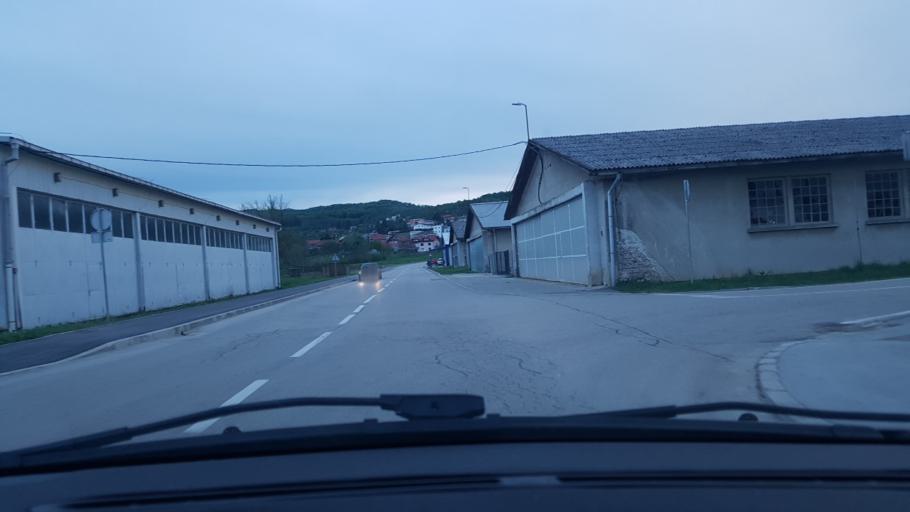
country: HR
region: Zagrebacka
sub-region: Grad Samobor
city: Samobor
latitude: 45.7942
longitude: 15.7238
